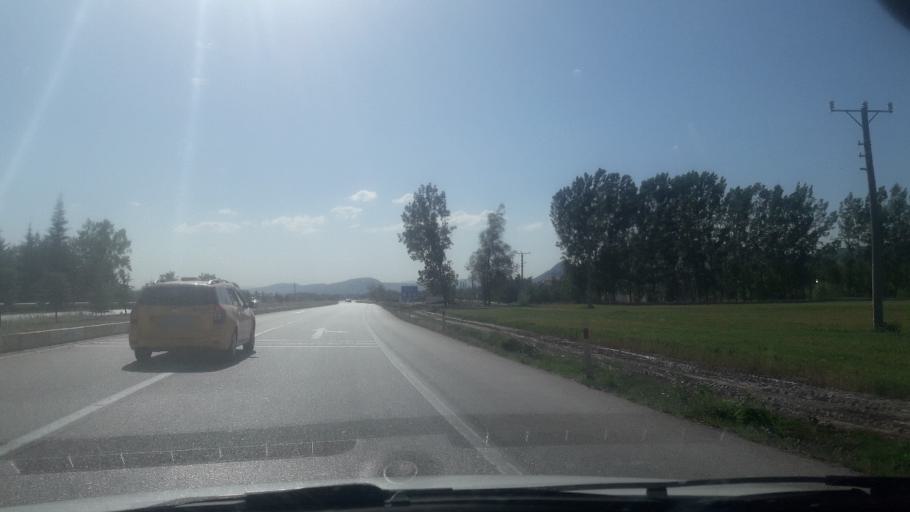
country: TR
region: Tokat
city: Dokmetepe
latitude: 40.3133
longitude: 36.2663
